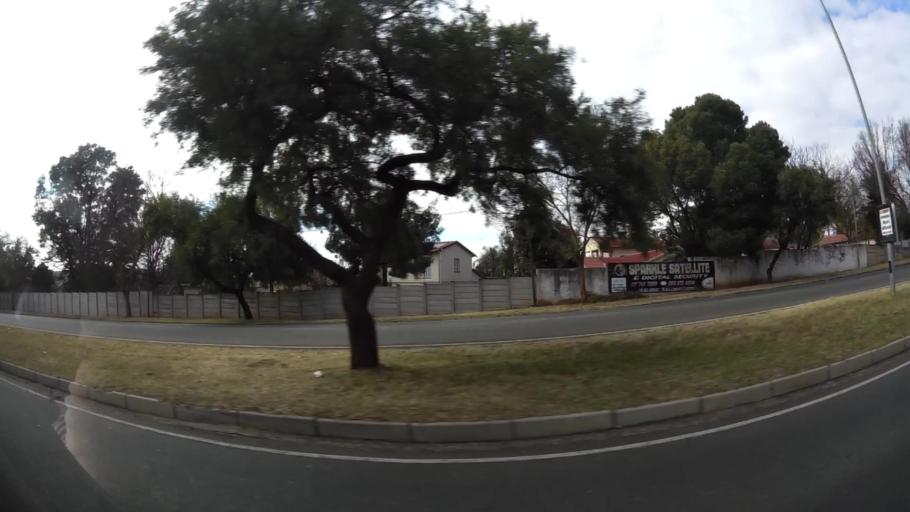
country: ZA
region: Gauteng
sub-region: City of Johannesburg Metropolitan Municipality
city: Roodepoort
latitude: -26.1142
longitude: 27.8523
